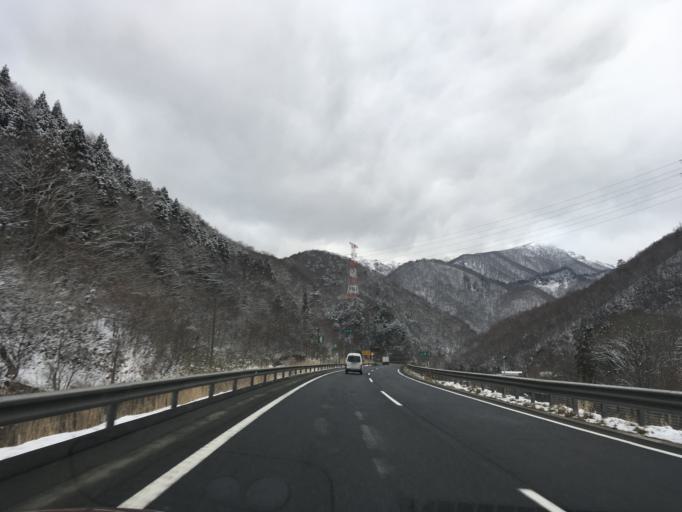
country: JP
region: Yamagata
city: Yamagata-shi
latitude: 38.2279
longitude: 140.4960
